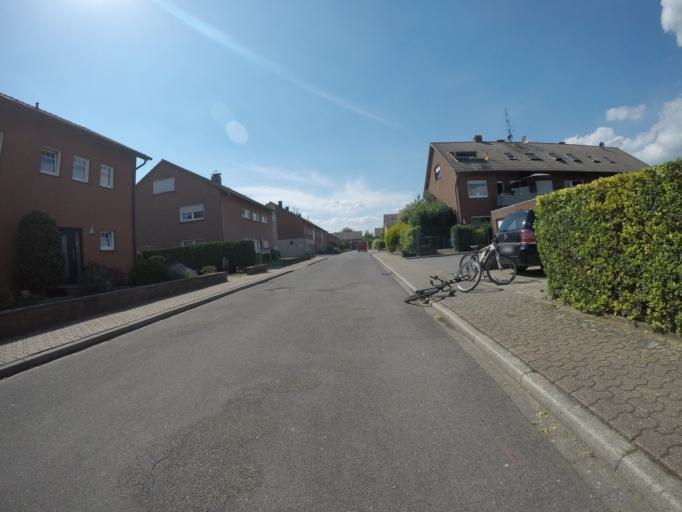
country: DE
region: North Rhine-Westphalia
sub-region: Regierungsbezirk Munster
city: Isselburg
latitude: 51.8502
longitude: 6.4272
